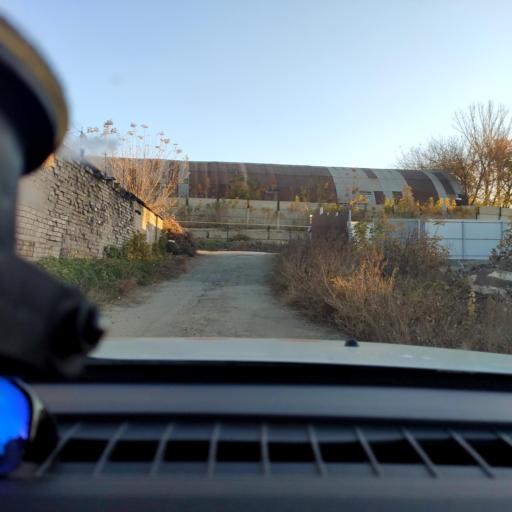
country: RU
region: Samara
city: Samara
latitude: 53.1816
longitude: 50.1506
